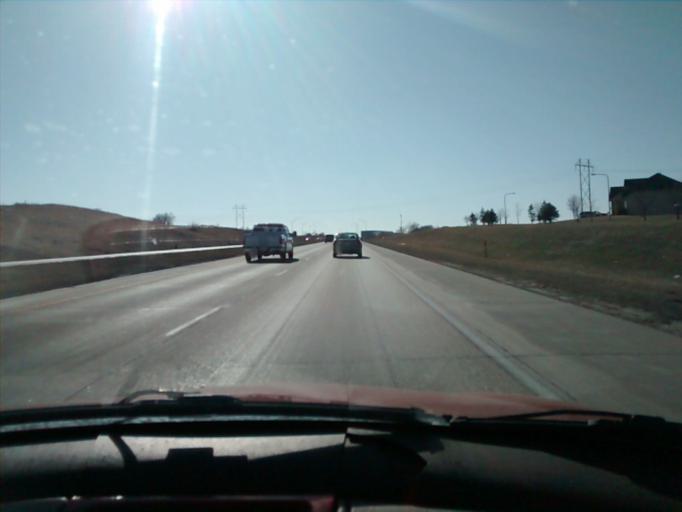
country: US
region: Nebraska
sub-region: Sarpy County
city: Papillion
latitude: 41.1384
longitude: -96.0091
